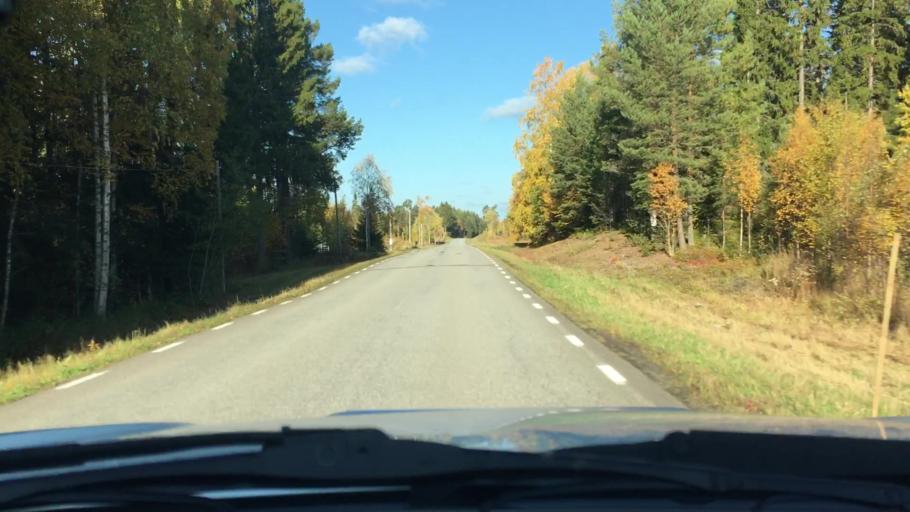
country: SE
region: Jaemtland
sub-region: Krokoms Kommun
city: Krokom
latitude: 63.3041
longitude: 14.2088
